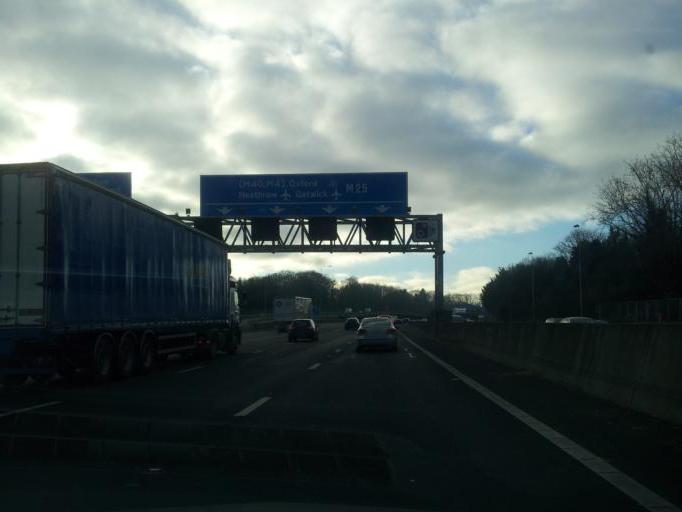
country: GB
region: England
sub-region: Hertfordshire
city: Chorleywood
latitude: 51.6593
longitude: -0.4941
